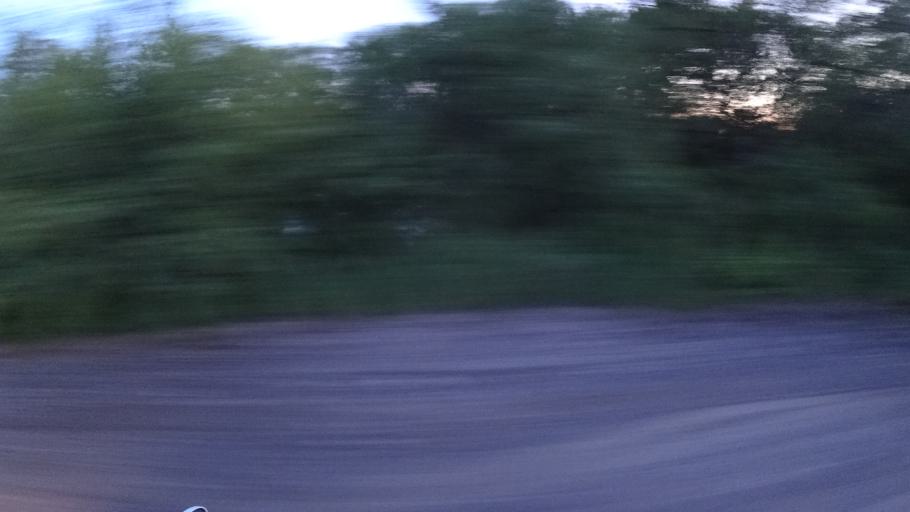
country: RU
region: Khabarovsk Krai
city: Khor
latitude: 47.8522
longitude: 134.9444
